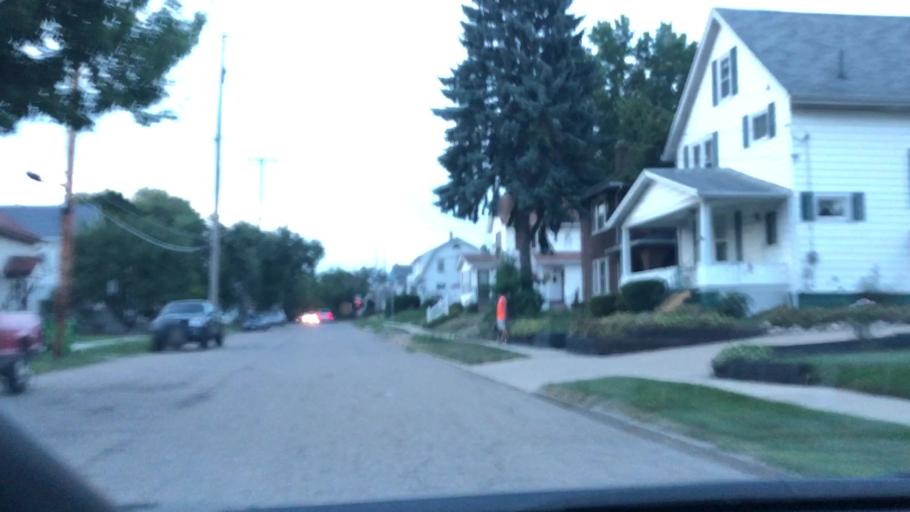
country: US
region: Ohio
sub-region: Stark County
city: Massillon
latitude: 40.8031
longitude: -81.5114
